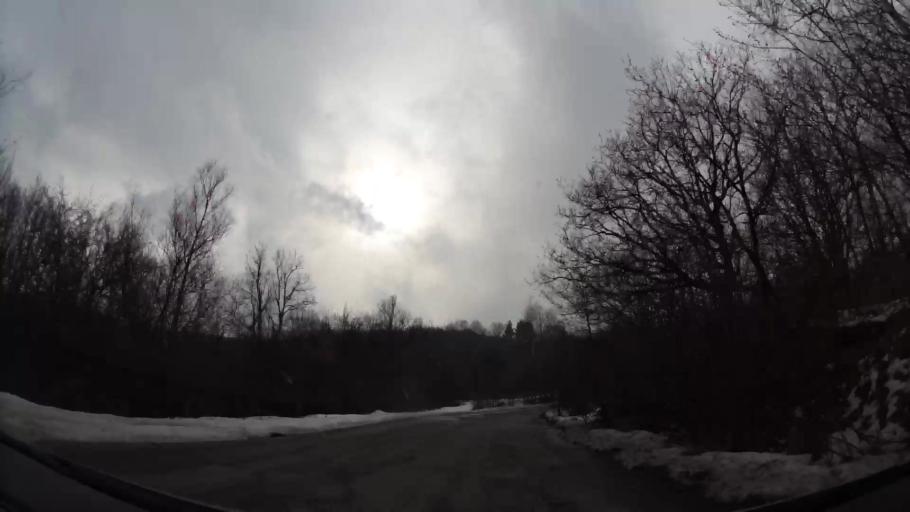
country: BG
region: Sofiya
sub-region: Obshtina Bozhurishte
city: Bozhurishte
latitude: 42.6576
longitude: 23.2055
